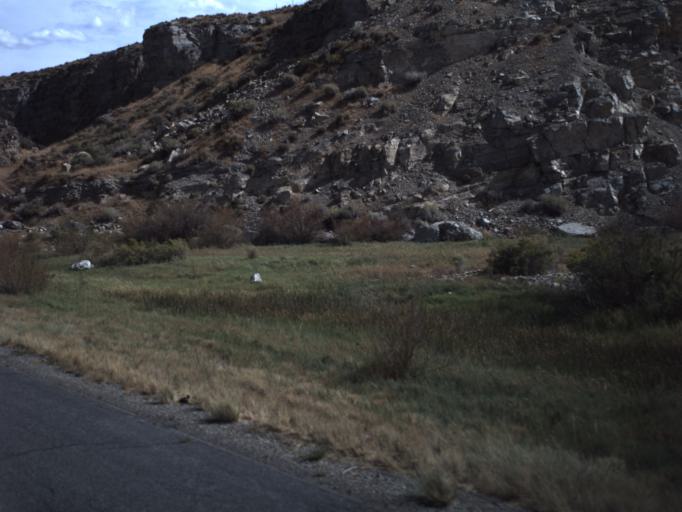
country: US
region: Utah
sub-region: Tooele County
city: Grantsville
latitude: 40.7443
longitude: -112.6370
